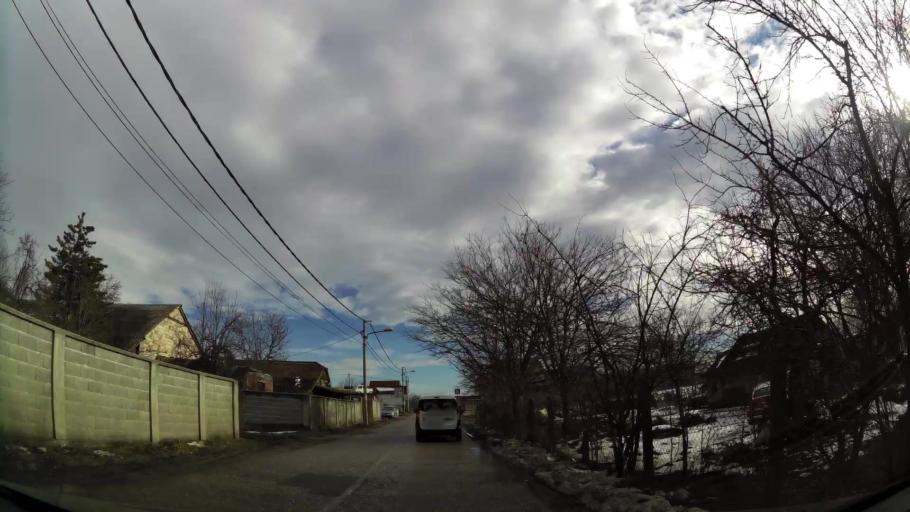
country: RS
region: Central Serbia
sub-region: Belgrade
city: Surcin
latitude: 44.7956
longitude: 20.3365
